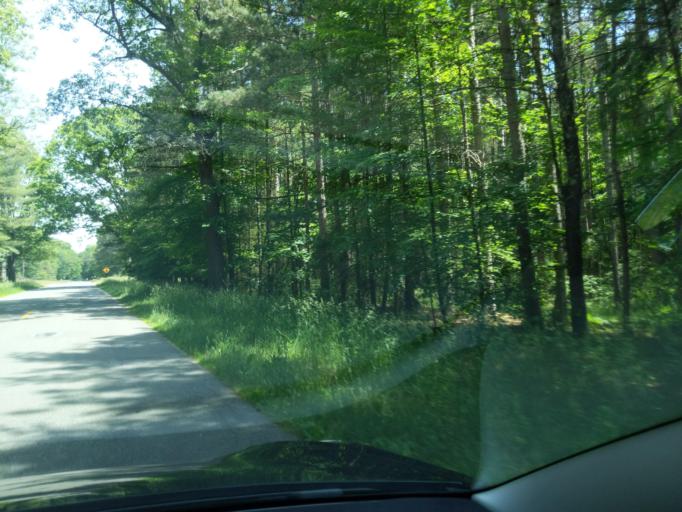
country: US
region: Michigan
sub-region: Muskegon County
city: Montague
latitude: 43.4158
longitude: -86.4005
